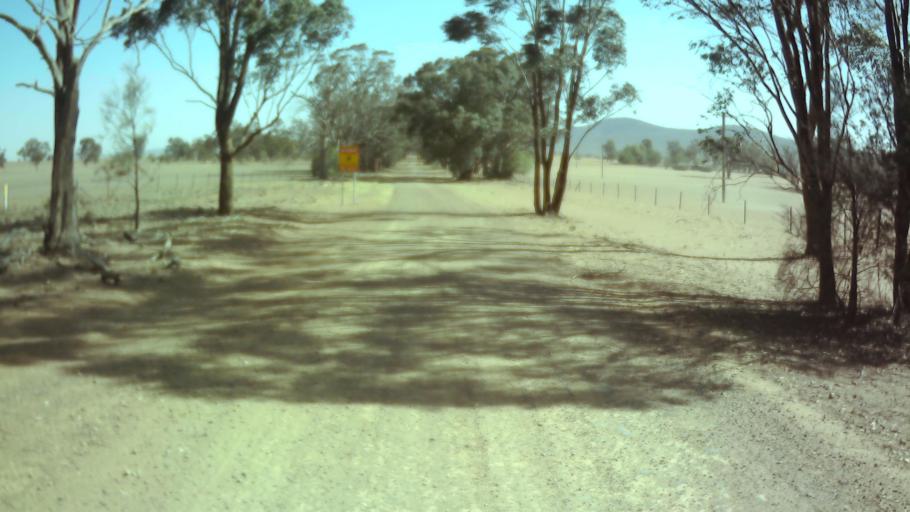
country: AU
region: New South Wales
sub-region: Weddin
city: Grenfell
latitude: -33.8419
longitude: 148.0179
